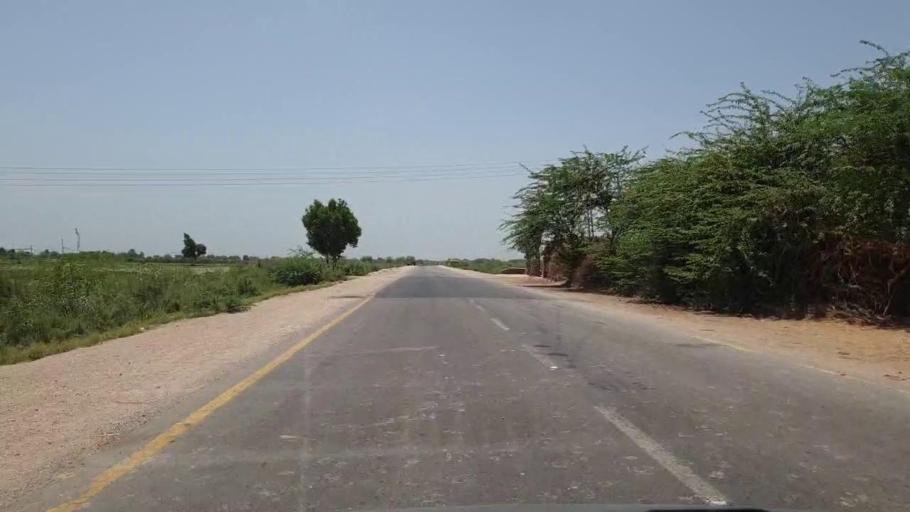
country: PK
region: Sindh
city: Sakrand
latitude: 26.1223
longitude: 68.3832
